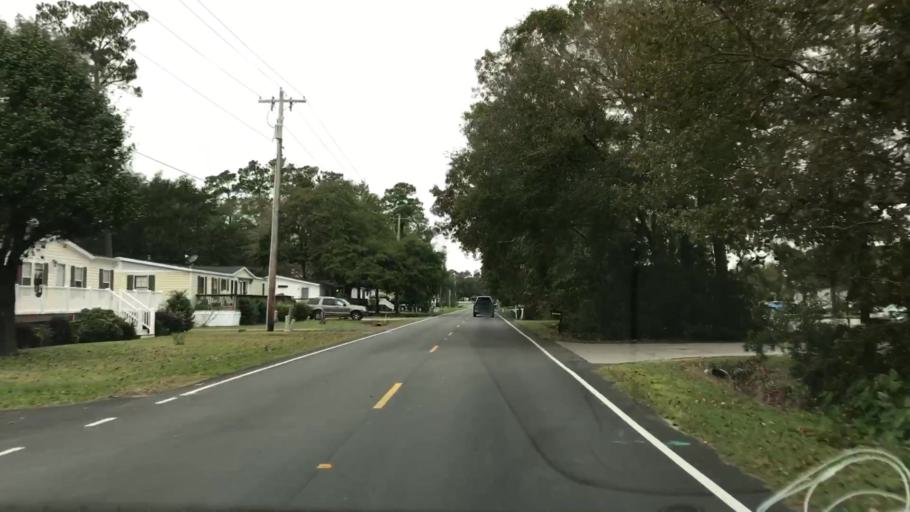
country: US
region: South Carolina
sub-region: Horry County
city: Garden City
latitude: 33.5876
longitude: -79.0030
